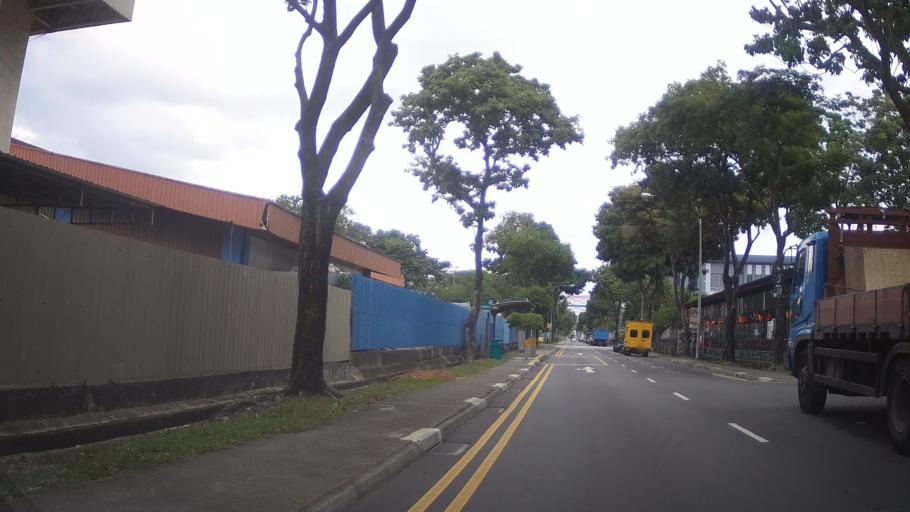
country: MY
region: Johor
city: Johor Bahru
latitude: 1.3255
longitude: 103.6688
